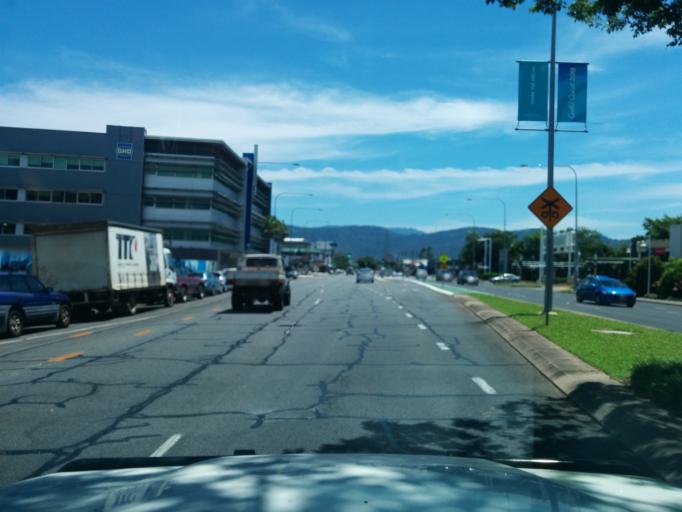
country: AU
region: Queensland
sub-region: Cairns
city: Cairns
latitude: -16.9266
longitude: 145.7737
